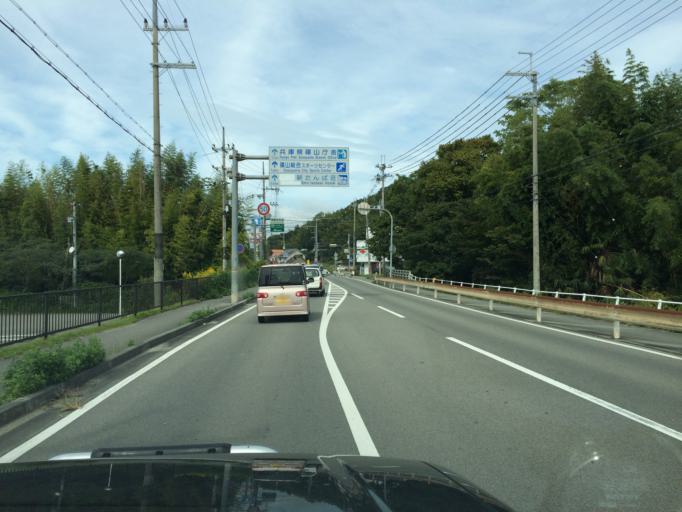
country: JP
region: Hyogo
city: Sasayama
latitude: 35.0742
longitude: 135.2065
